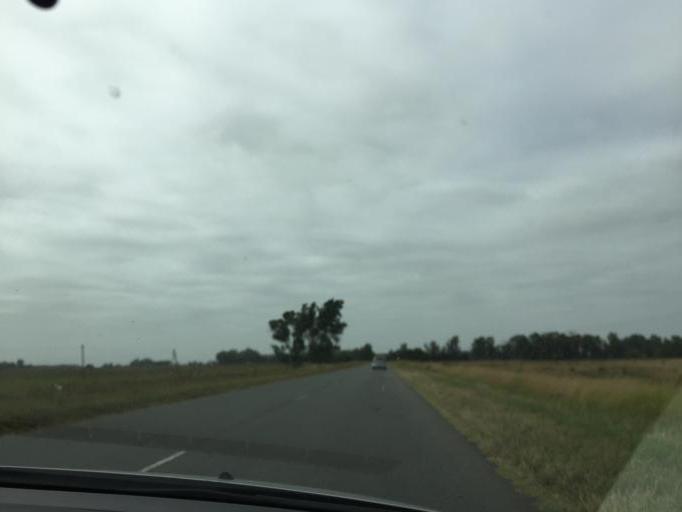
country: AR
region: Buenos Aires
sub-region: Partido de Las Flores
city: Las Flores
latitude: -36.1974
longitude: -59.0532
